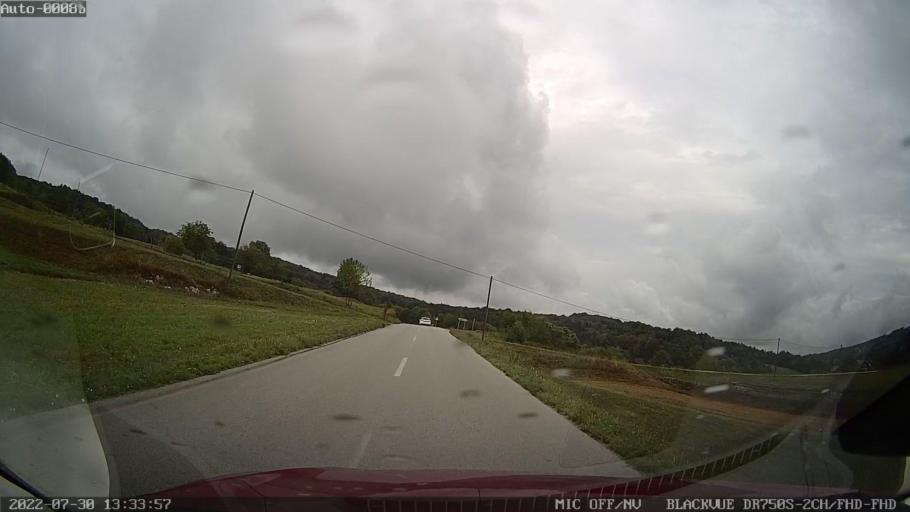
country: SI
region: Zuzemberk
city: Zuzemberk
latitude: 45.8552
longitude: 14.9339
